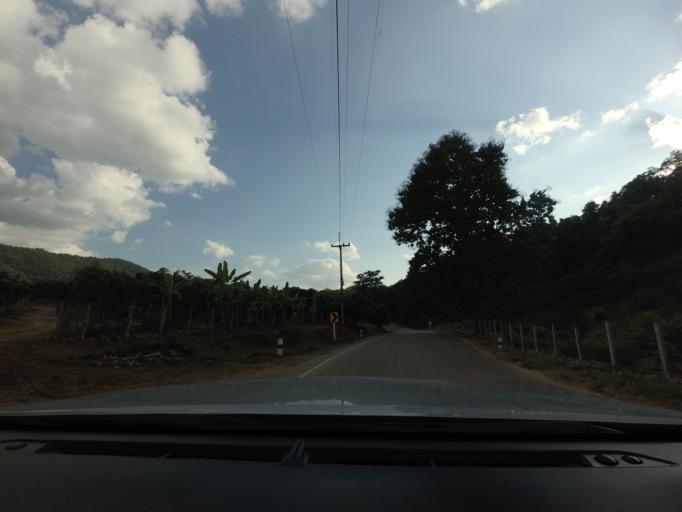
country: TH
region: Chiang Mai
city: Chai Prakan
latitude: 19.6398
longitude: 99.1620
